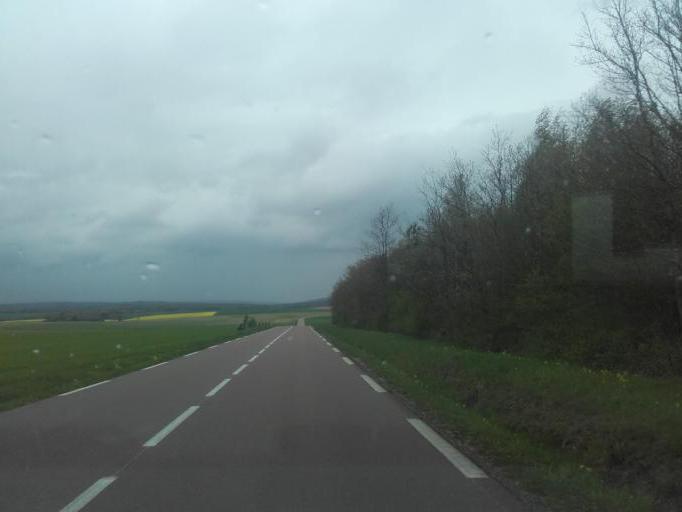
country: FR
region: Bourgogne
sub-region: Departement de l'Yonne
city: Joux-la-Ville
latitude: 47.7058
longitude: 3.8566
